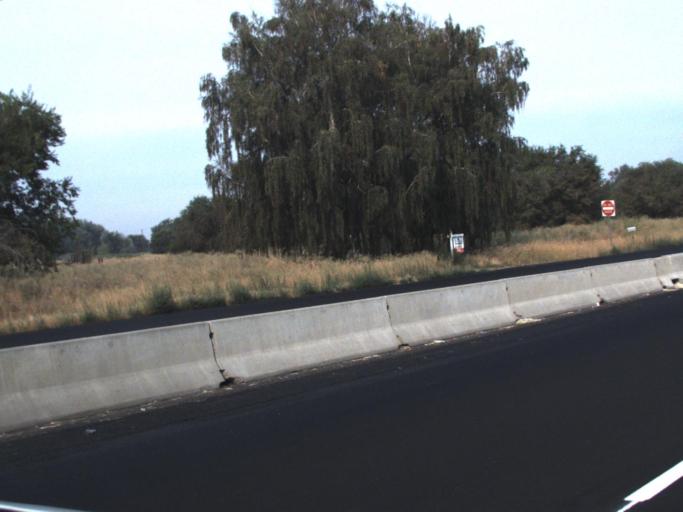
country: US
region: Washington
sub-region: Yakima County
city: Toppenish
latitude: 46.3980
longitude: -120.3701
